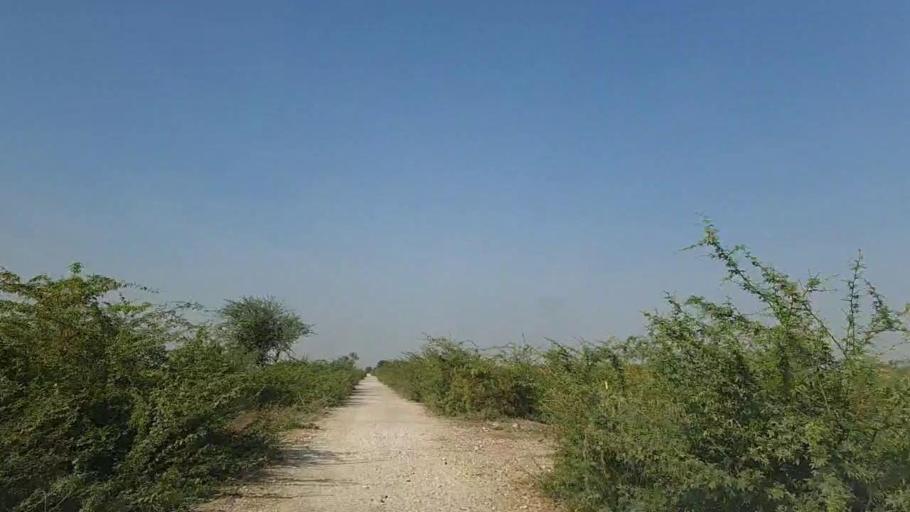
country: PK
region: Sindh
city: Naukot
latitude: 24.9202
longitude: 69.4878
